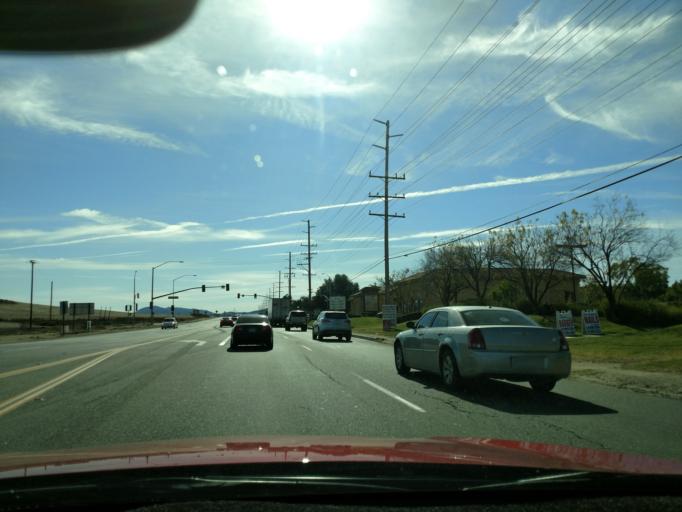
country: US
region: California
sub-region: Riverside County
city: Murrieta Hot Springs
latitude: 33.5701
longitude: -117.1363
